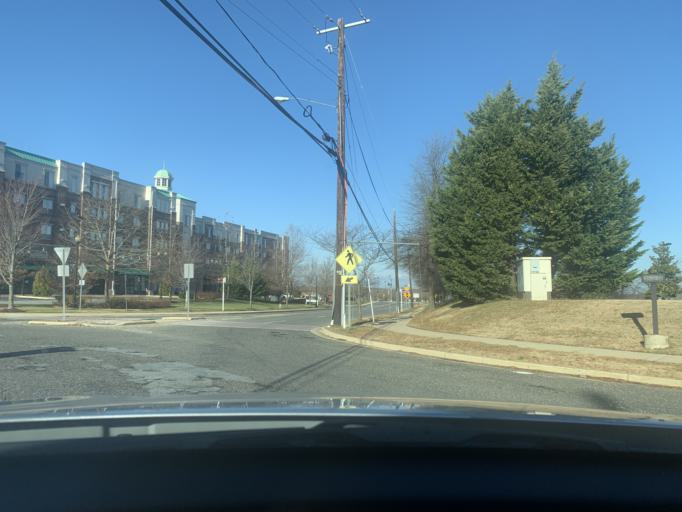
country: US
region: Maryland
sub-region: Prince George's County
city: Camp Springs
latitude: 38.8242
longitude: -76.9117
